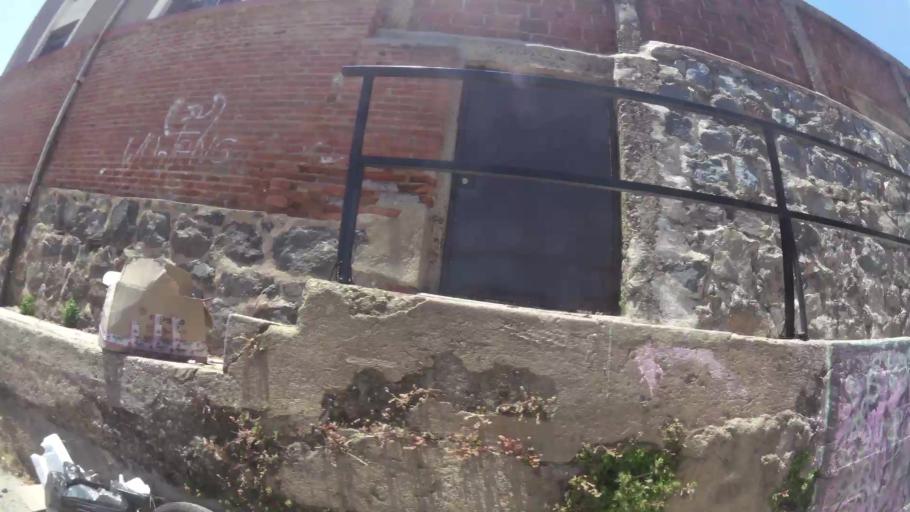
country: CL
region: Valparaiso
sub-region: Provincia de Valparaiso
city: Valparaiso
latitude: -33.0416
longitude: -71.6354
